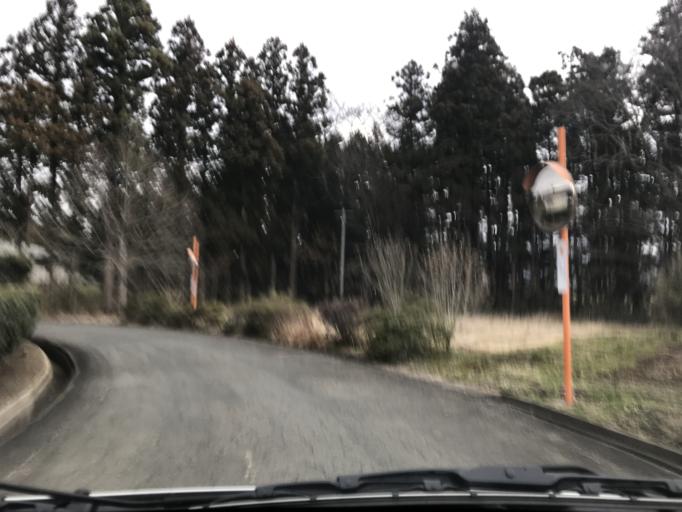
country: JP
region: Iwate
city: Mizusawa
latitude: 39.0844
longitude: 141.1730
